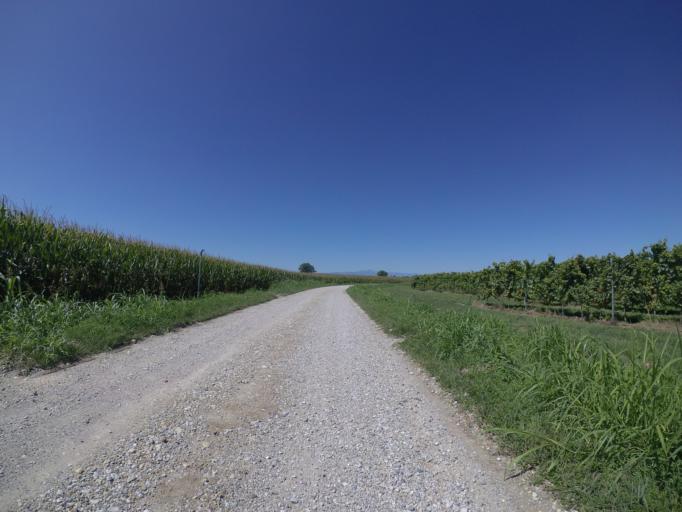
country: IT
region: Friuli Venezia Giulia
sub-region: Provincia di Udine
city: Varmo
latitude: 45.8658
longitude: 13.0101
